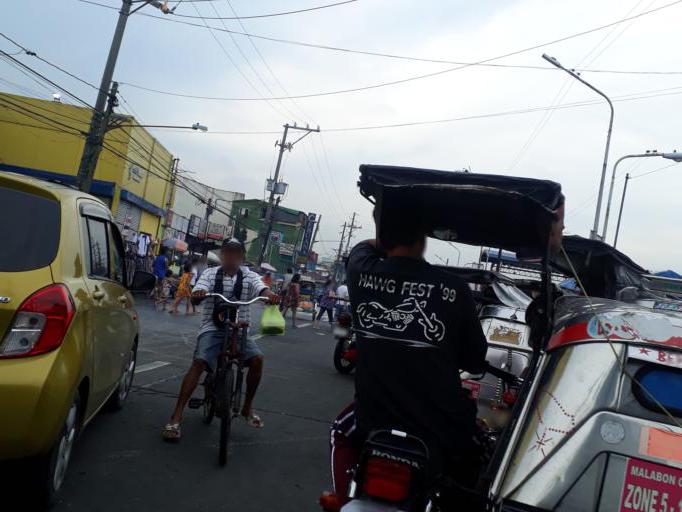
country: PH
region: Metro Manila
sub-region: Caloocan City
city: Niugan
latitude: 14.6573
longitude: 120.9511
